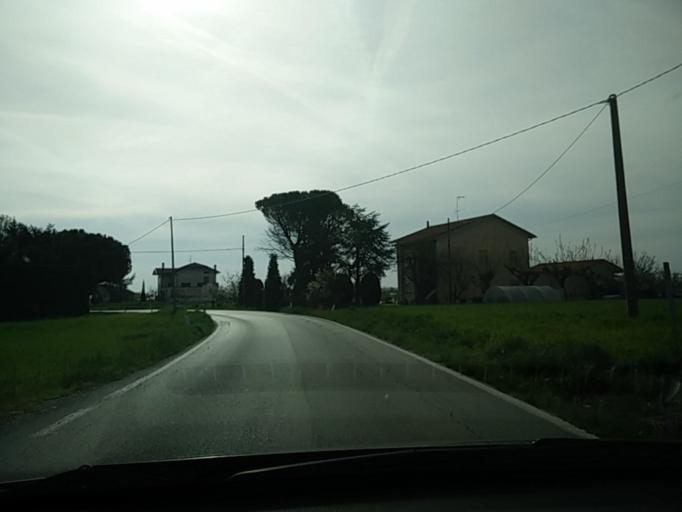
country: IT
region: Emilia-Romagna
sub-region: Provincia di Rimini
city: Santa Giustina
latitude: 44.0823
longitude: 12.4894
